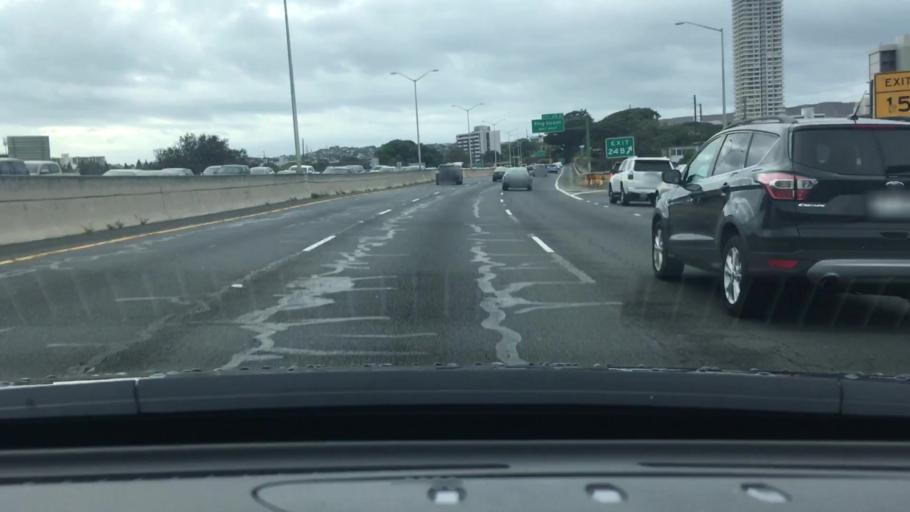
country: US
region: Hawaii
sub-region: Honolulu County
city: Honolulu
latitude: 21.2940
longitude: -157.8207
